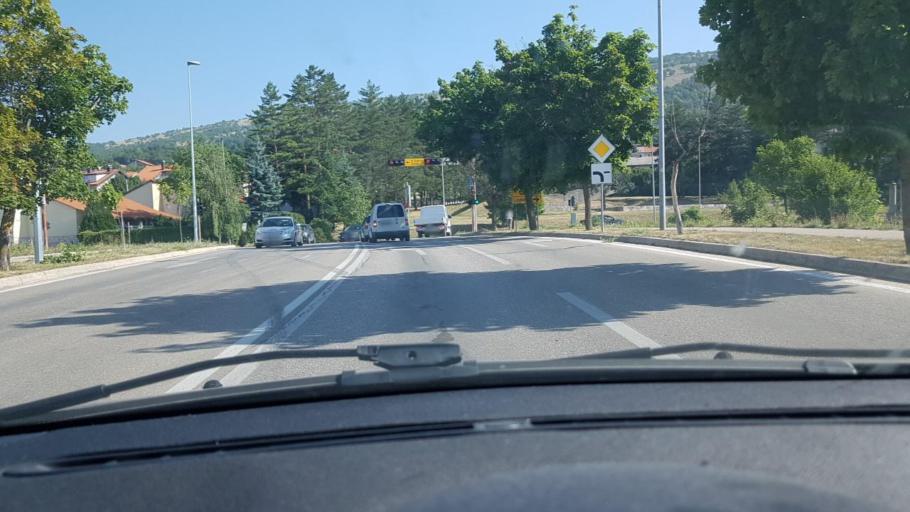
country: BA
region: Federation of Bosnia and Herzegovina
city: Livno
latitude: 43.8283
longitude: 16.9975
